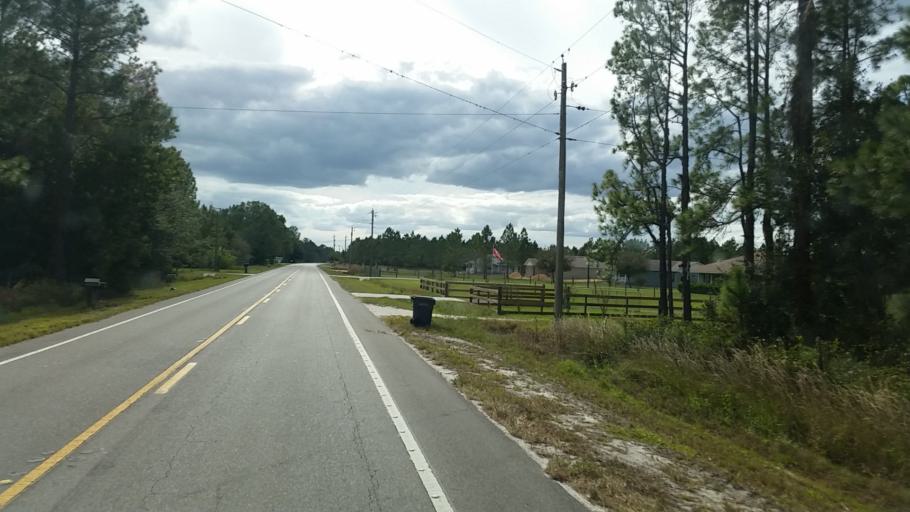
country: US
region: Florida
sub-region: Polk County
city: Gibsonia
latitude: 28.2501
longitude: -81.9670
